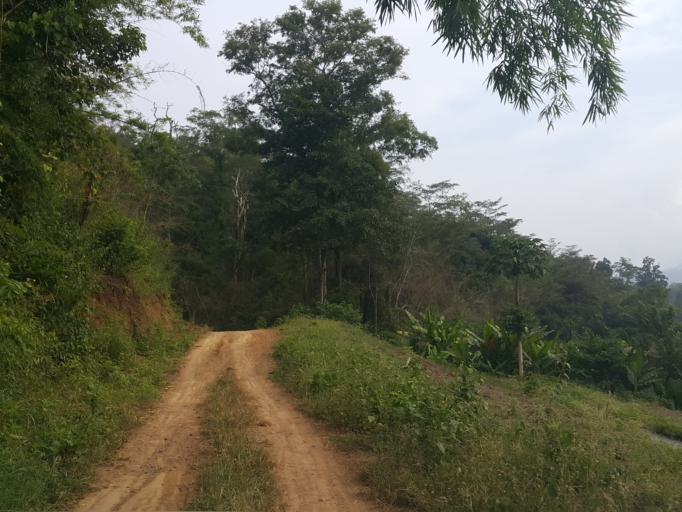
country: TH
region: Mae Hong Son
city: Wiang Nuea
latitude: 19.3985
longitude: 98.4736
